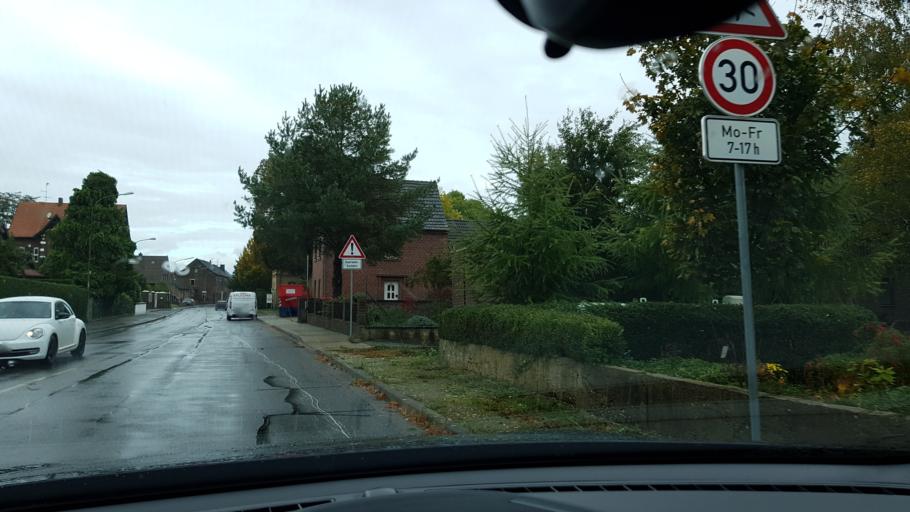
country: DE
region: North Rhine-Westphalia
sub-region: Regierungsbezirk Dusseldorf
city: Rommerskirchen
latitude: 51.0710
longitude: 6.6955
